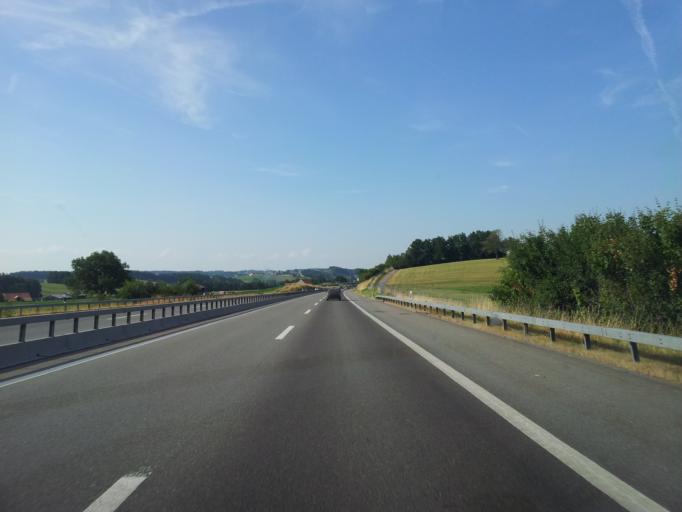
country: CH
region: Fribourg
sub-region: Veveyse District
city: Chatel-Saint-Denis
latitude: 46.5499
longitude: 6.9153
